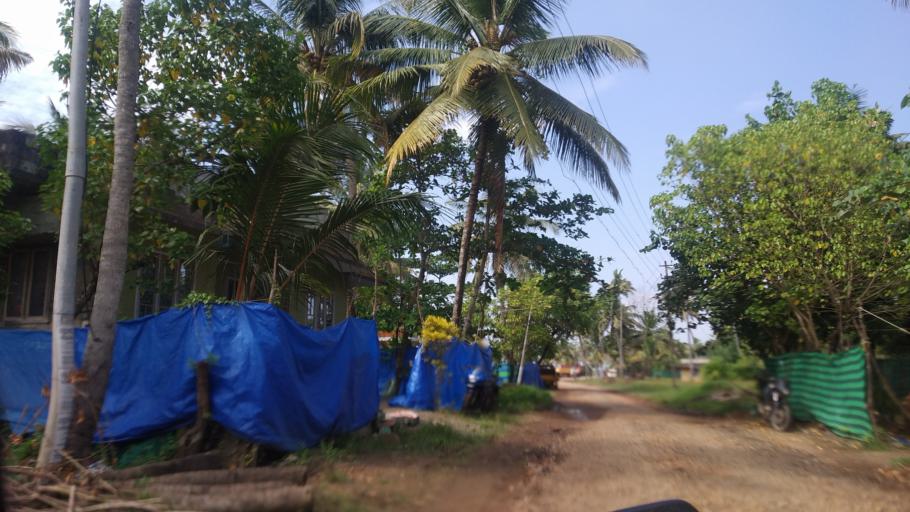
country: IN
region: Kerala
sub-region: Ernakulam
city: Elur
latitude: 10.0581
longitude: 76.2010
